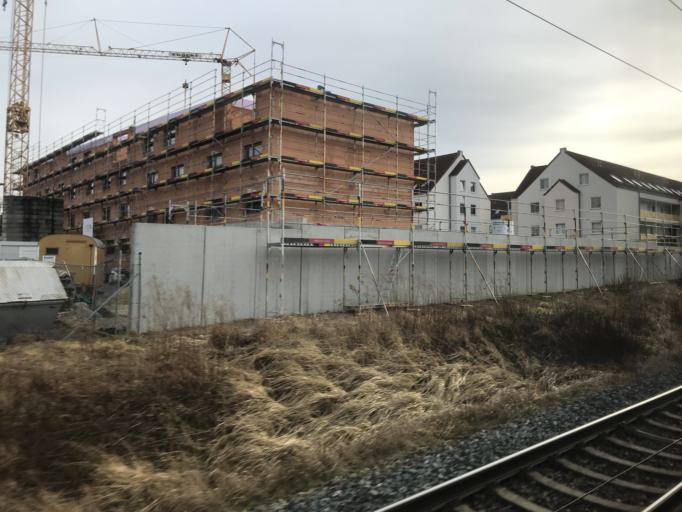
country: DE
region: Bavaria
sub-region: Swabia
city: Diedorf
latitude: 48.3507
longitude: 10.7694
